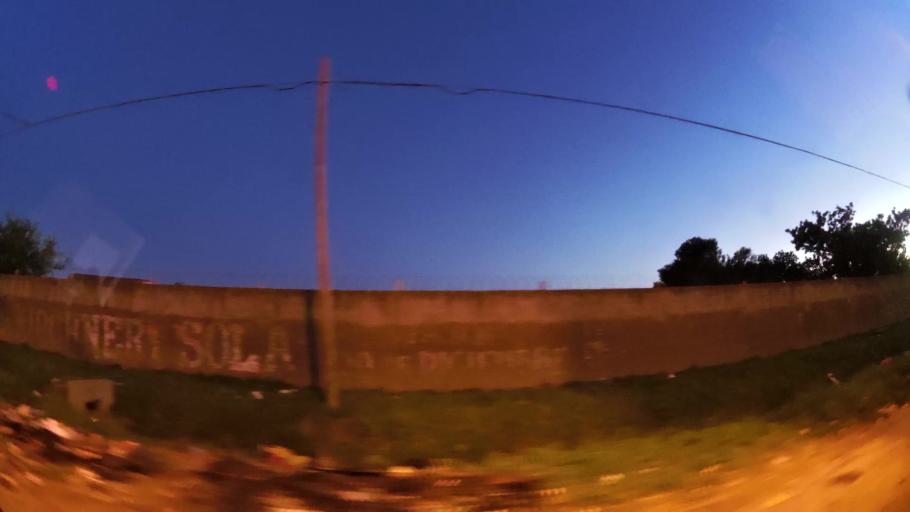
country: AR
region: Buenos Aires
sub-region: Partido de Almirante Brown
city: Adrogue
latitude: -34.7527
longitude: -58.3345
